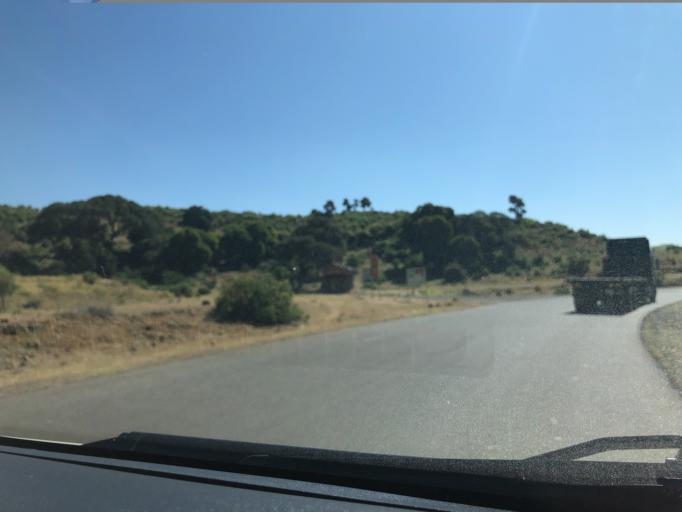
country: ET
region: Amhara
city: Adis Zemen
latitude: 12.2274
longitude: 37.6321
